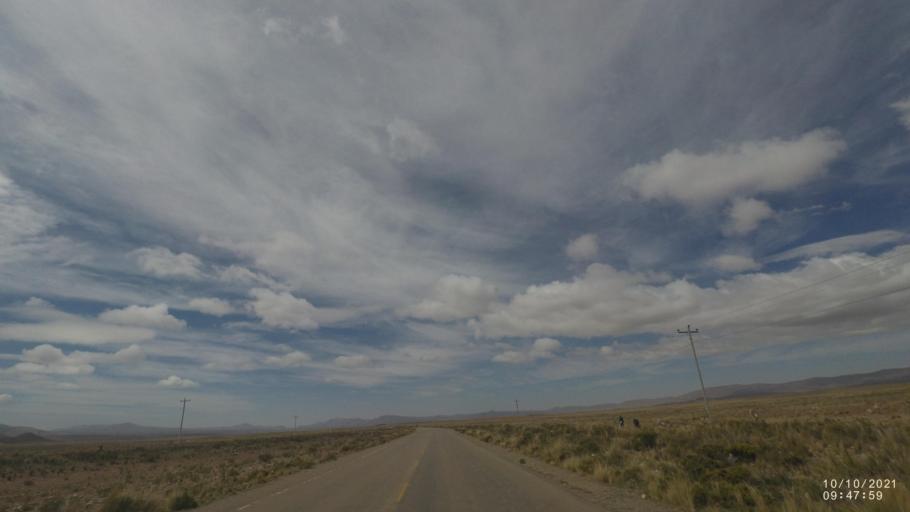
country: BO
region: La Paz
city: Quime
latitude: -17.2022
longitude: -67.3423
